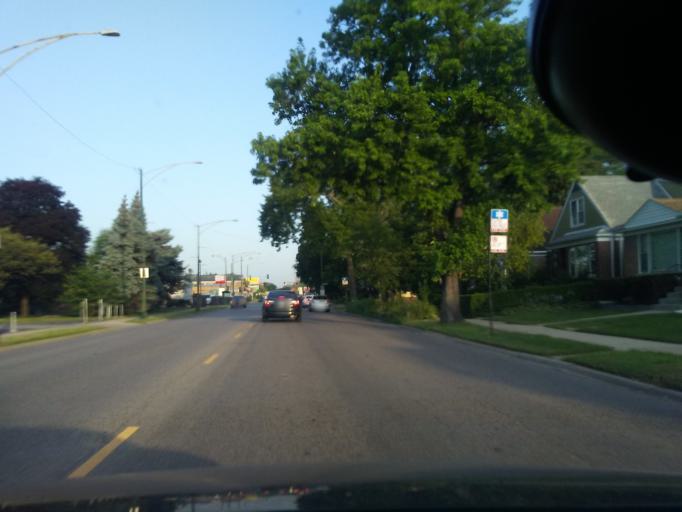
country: US
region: Illinois
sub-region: Cook County
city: Lincolnwood
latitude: 41.9754
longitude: -87.7497
